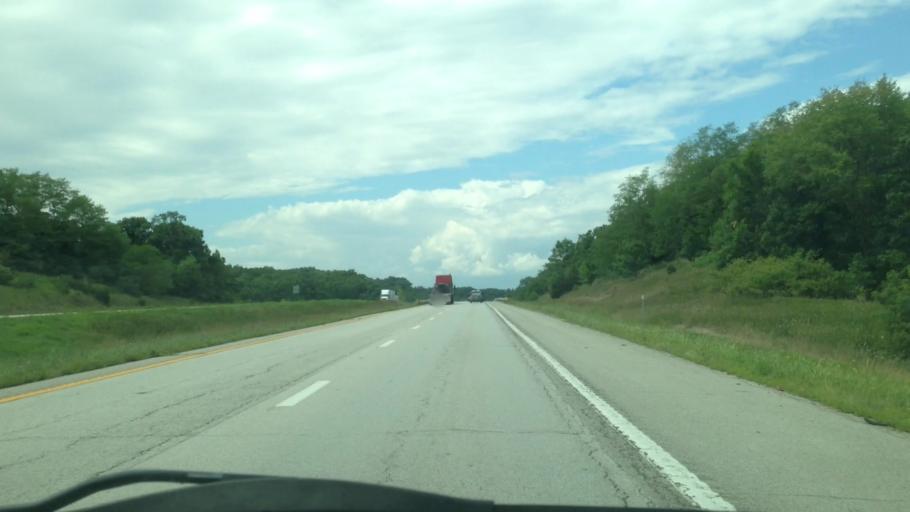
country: US
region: Missouri
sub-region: Pike County
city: Bowling Green
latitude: 39.3517
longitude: -91.1915
